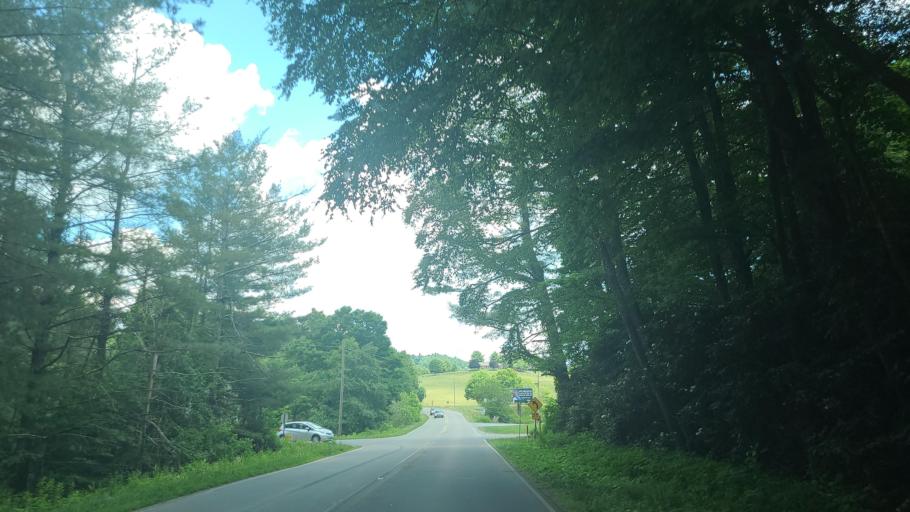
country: US
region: North Carolina
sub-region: Watauga County
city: Boone
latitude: 36.2335
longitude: -81.5509
